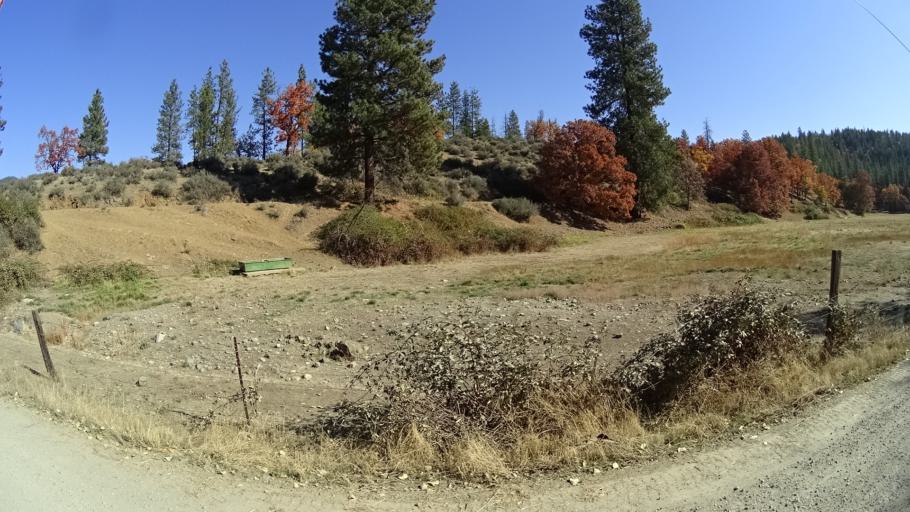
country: US
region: California
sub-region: Siskiyou County
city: Yreka
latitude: 41.6236
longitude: -122.9652
